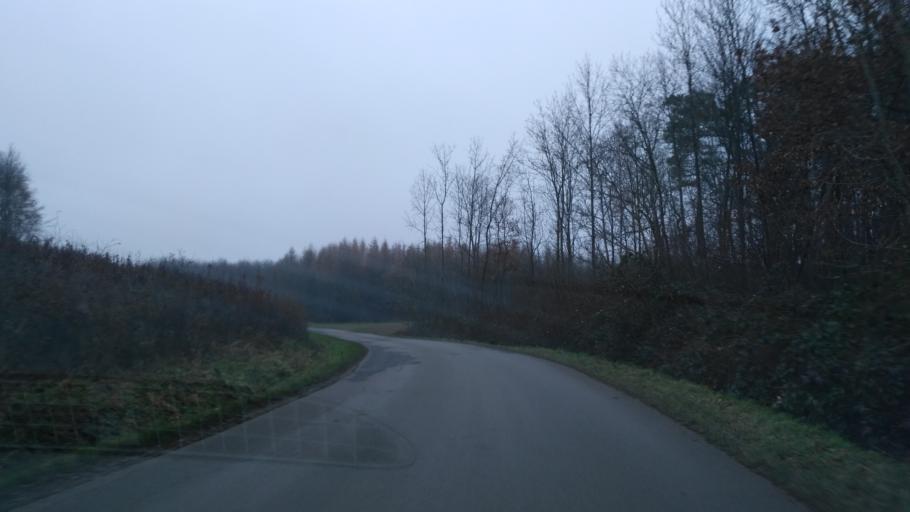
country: PL
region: Subcarpathian Voivodeship
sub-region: Powiat przeworski
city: Zurawiczki
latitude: 49.9976
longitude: 22.5150
